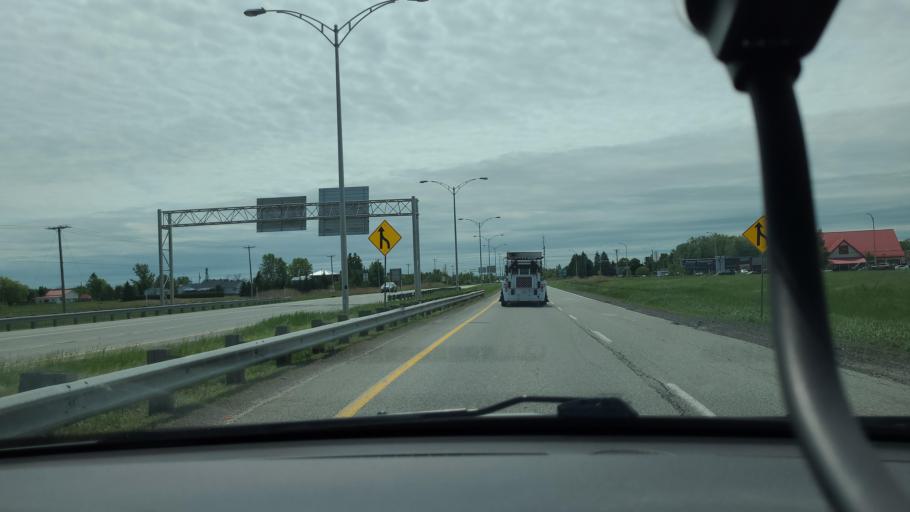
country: CA
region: Quebec
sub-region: Lanaudiere
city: Sainte-Julienne
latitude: 45.9039
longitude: -73.6590
